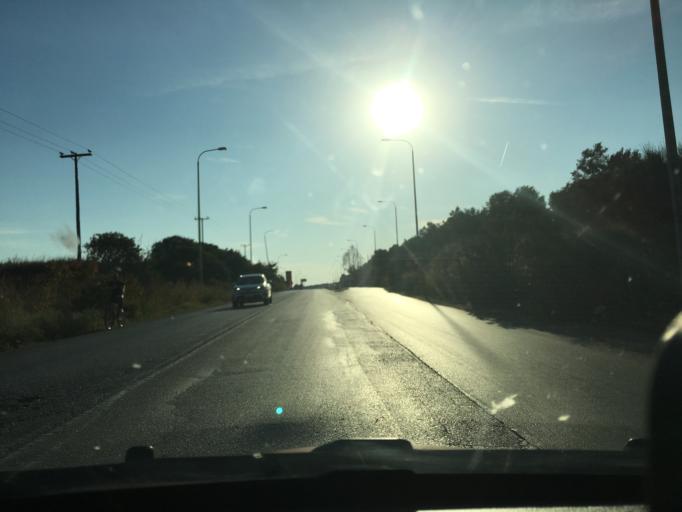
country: GR
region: Central Macedonia
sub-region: Nomos Chalkidikis
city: Nea Moudhania
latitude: 40.2466
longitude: 23.3067
